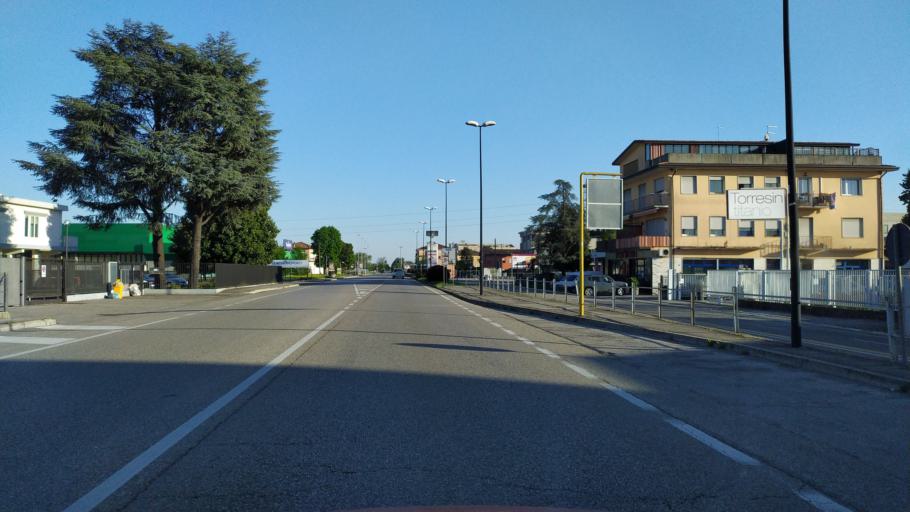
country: IT
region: Veneto
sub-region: Provincia di Padova
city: Limena
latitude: 45.4590
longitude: 11.8548
